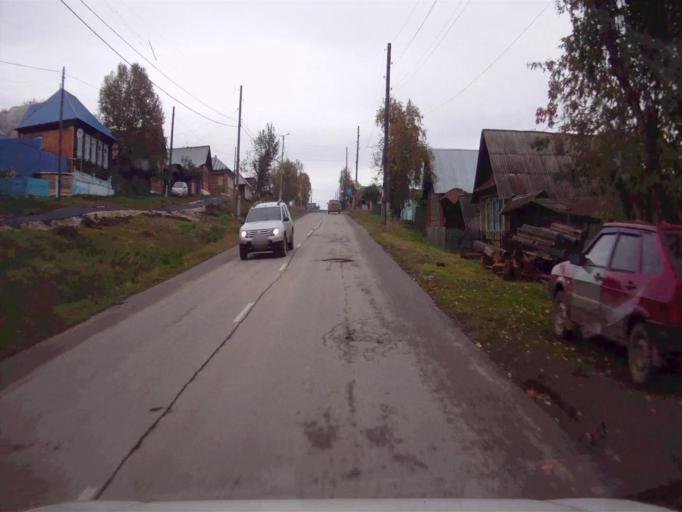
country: RU
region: Chelyabinsk
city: Nyazepetrovsk
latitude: 56.0580
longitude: 59.6089
